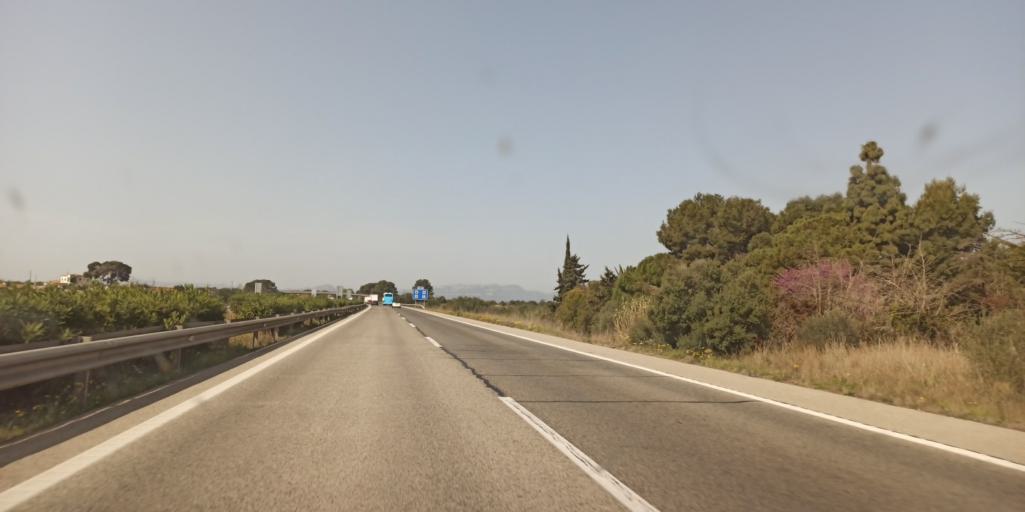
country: ES
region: Catalonia
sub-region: Provincia de Tarragona
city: Salou
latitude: 41.1012
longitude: 1.1096
